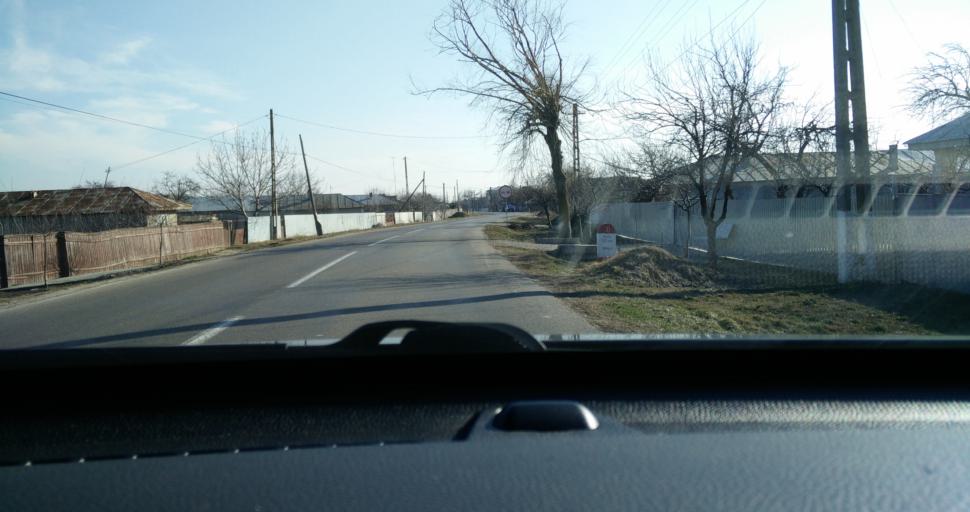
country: RO
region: Vrancea
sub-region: Comuna Nanesti
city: Nanesti
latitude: 45.5541
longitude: 27.5001
